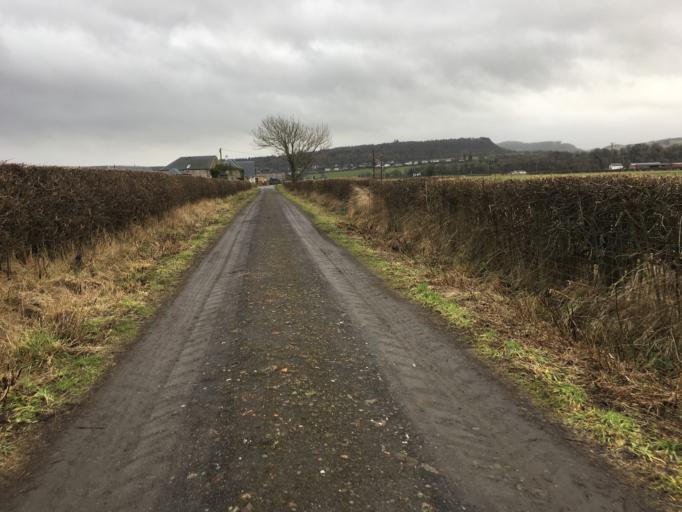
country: GB
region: Scotland
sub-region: Stirling
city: Stirling
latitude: 56.1245
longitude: -3.9761
